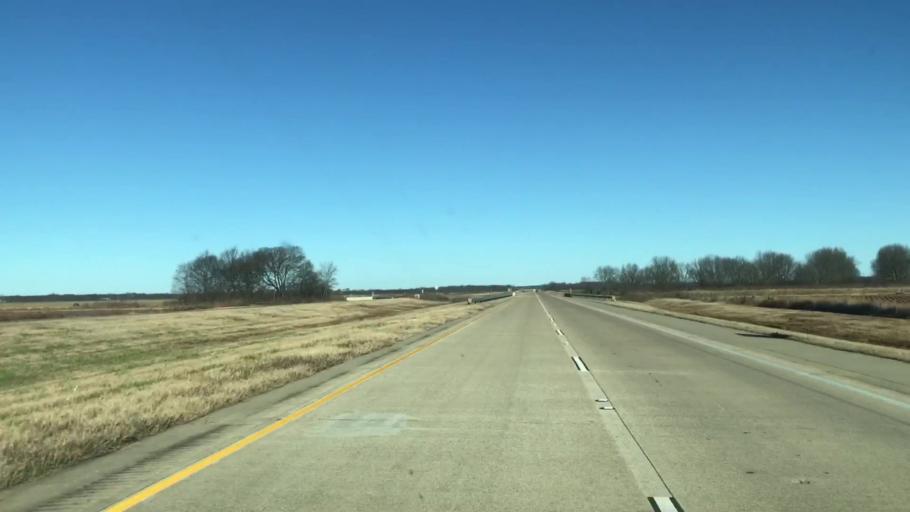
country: US
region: Louisiana
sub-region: Caddo Parish
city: Oil City
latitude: 32.7182
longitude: -93.8682
